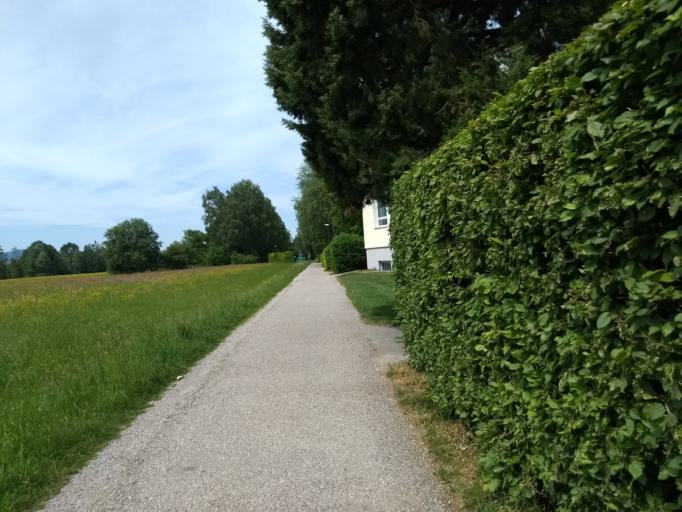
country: AT
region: Salzburg
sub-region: Salzburg Stadt
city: Salzburg
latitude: 47.7810
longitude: 13.0227
